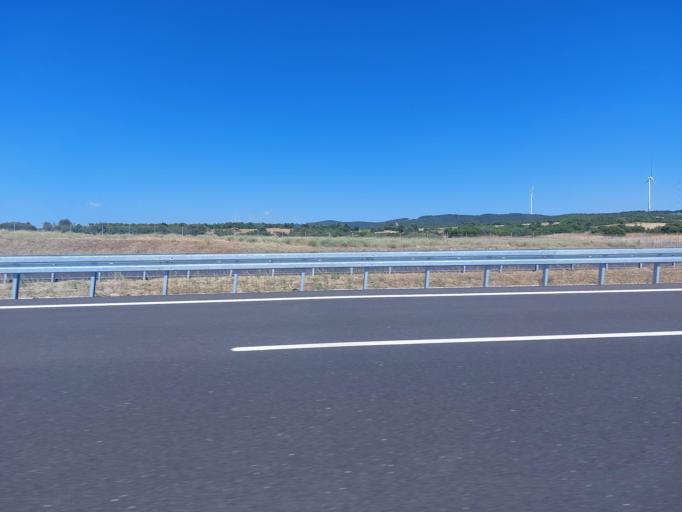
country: TR
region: Tekirdag
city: Balli
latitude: 40.7410
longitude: 26.9904
